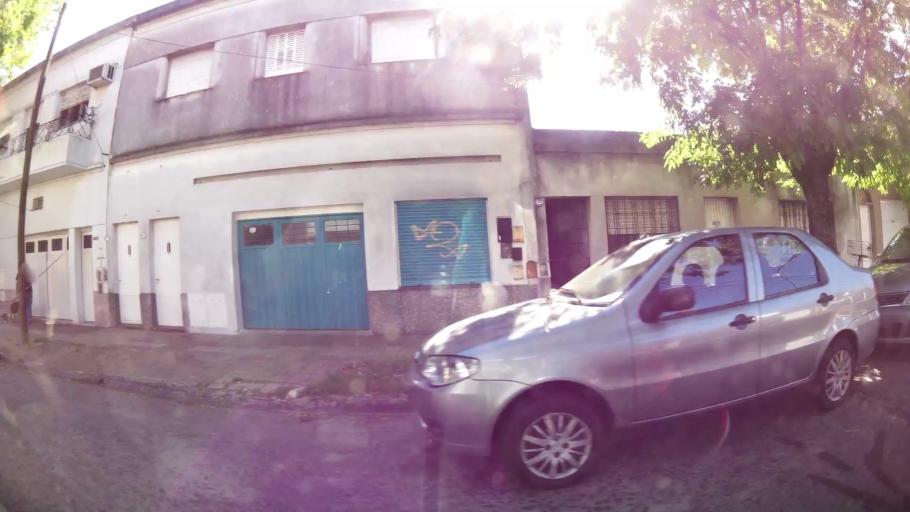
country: AR
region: Buenos Aires
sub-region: Partido de General San Martin
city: General San Martin
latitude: -34.5457
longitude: -58.5033
